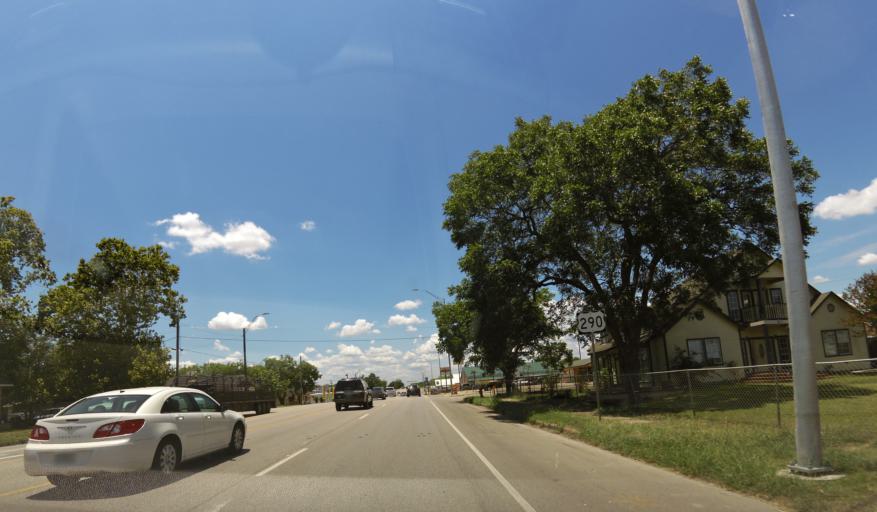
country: US
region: Texas
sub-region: Lee County
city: Giddings
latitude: 30.1836
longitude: -96.9409
